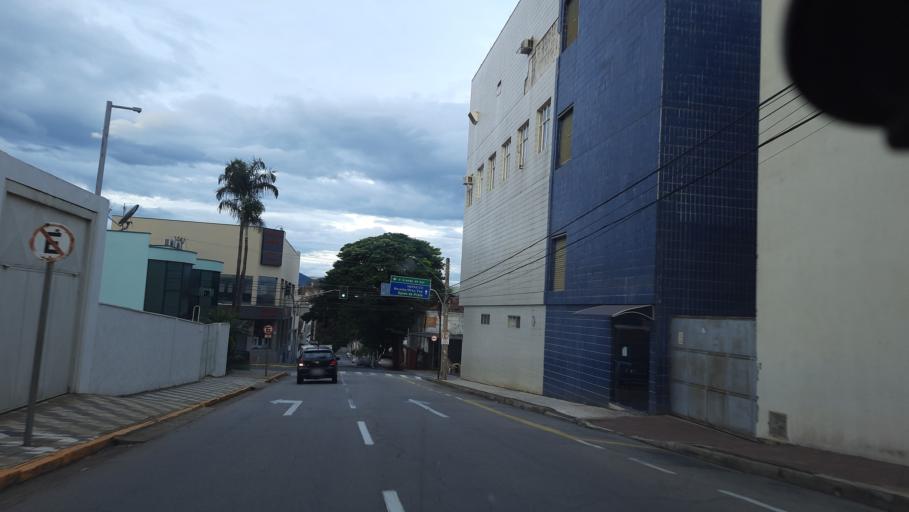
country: BR
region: Sao Paulo
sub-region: Sao Joao Da Boa Vista
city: Sao Joao da Boa Vista
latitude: -21.9685
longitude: -46.7963
